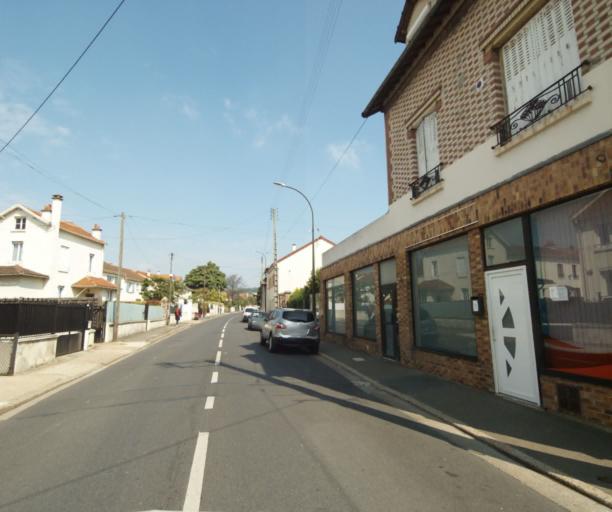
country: FR
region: Ile-de-France
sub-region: Departement du Val-d'Oise
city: Argenteuil
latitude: 48.9559
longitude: 2.2413
